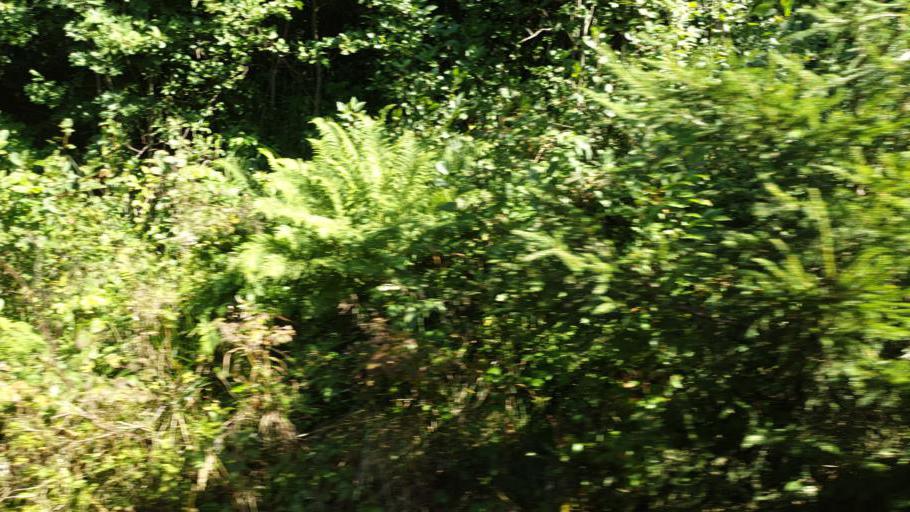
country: NO
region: Sor-Trondelag
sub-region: Meldal
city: Meldal
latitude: 63.1733
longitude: 9.7492
